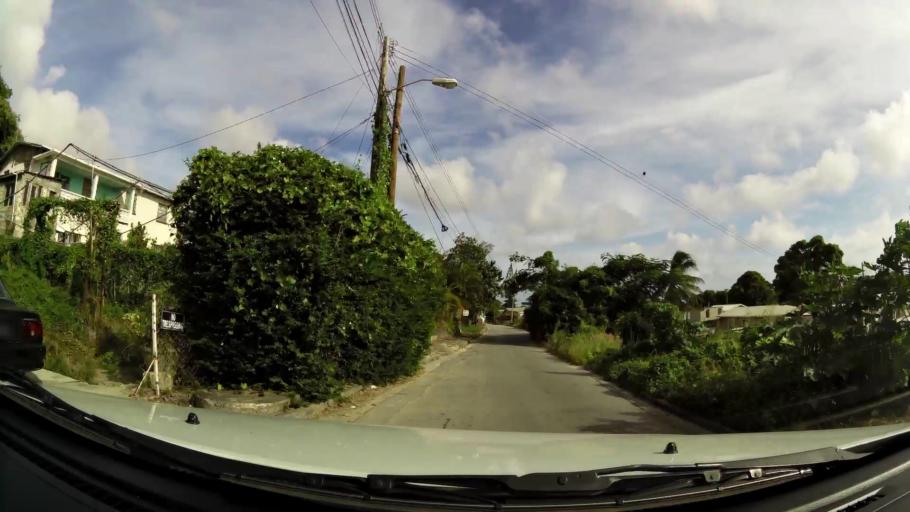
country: BB
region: Saint Michael
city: Bridgetown
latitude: 13.0876
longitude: -59.5897
